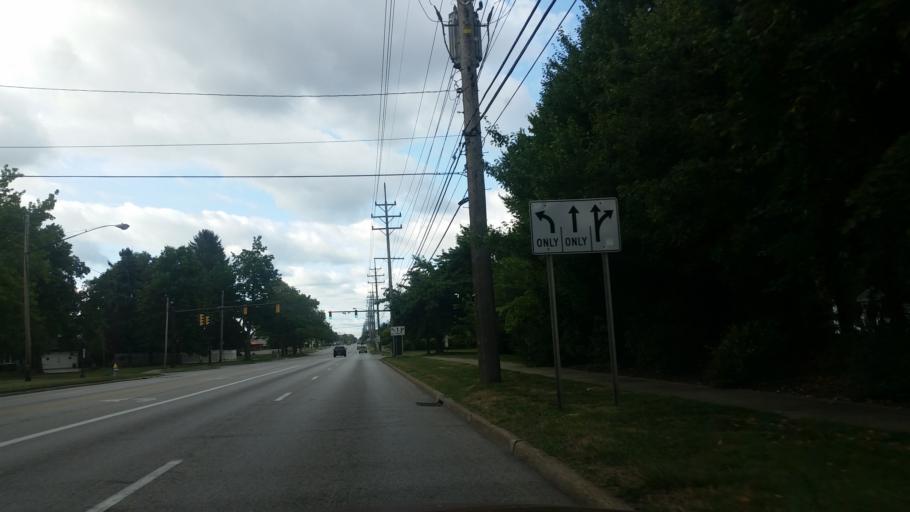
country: US
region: Ohio
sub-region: Cuyahoga County
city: Brook Park
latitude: 41.3846
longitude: -81.7847
